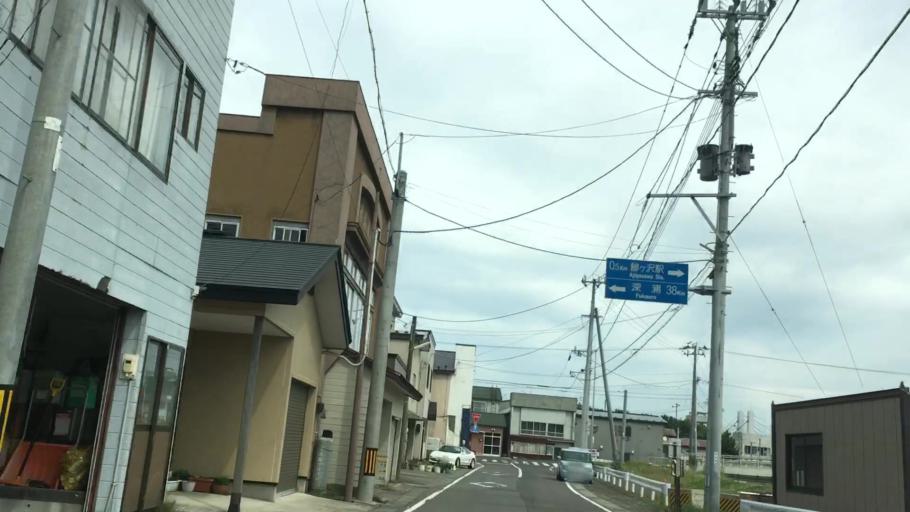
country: JP
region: Aomori
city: Shimokizukuri
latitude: 40.7772
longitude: 140.2173
